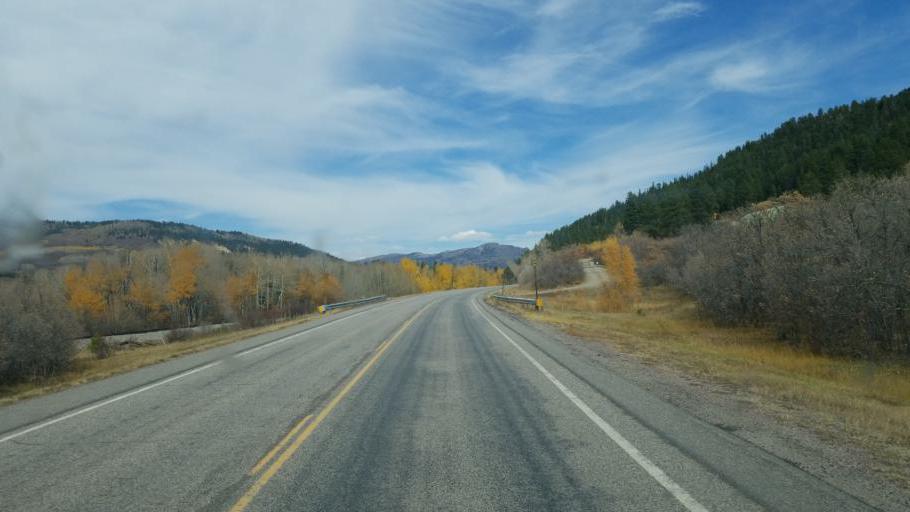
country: US
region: New Mexico
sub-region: Rio Arriba County
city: Chama
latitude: 36.9271
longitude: -106.5580
